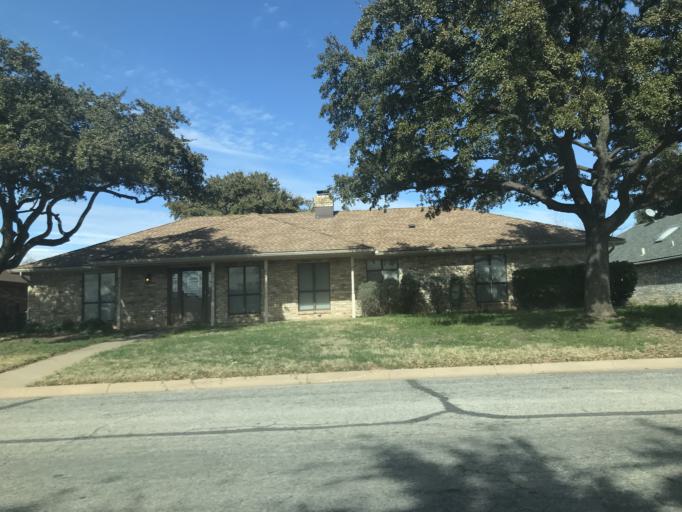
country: US
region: Texas
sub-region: Tom Green County
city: San Angelo
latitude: 31.4255
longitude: -100.4949
